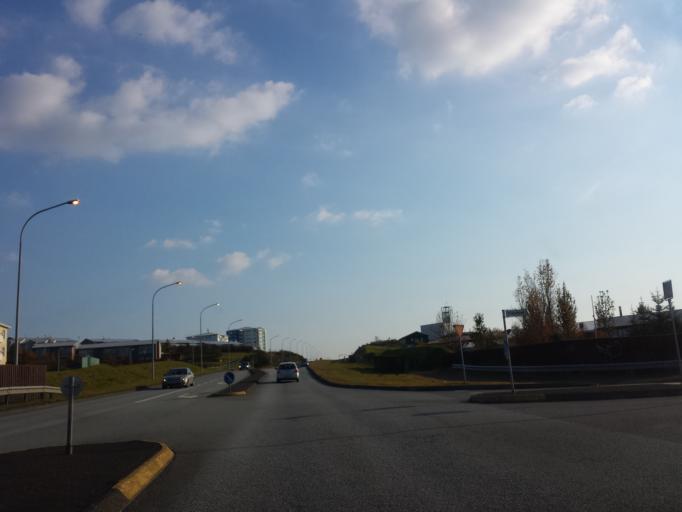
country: IS
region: Capital Region
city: Reykjavik
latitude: 64.0976
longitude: -21.8682
